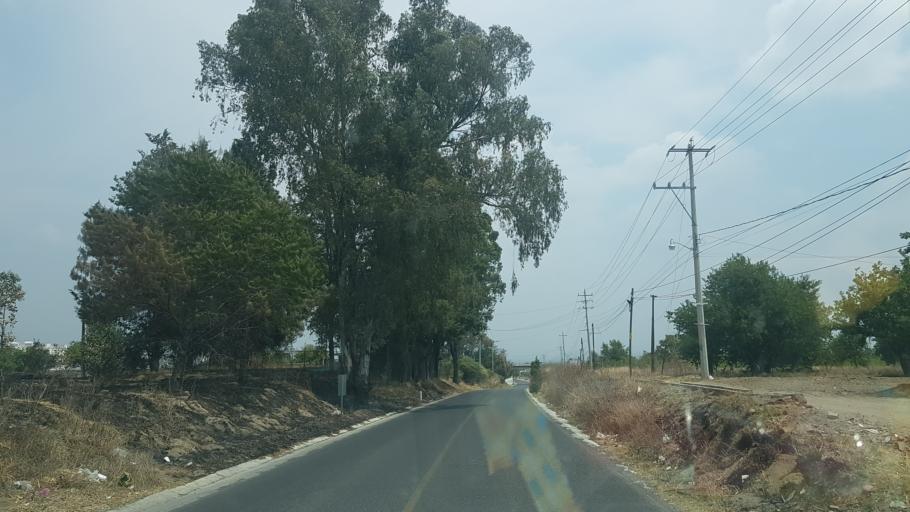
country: MX
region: Puebla
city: Huejotzingo
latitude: 19.1409
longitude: -98.4122
